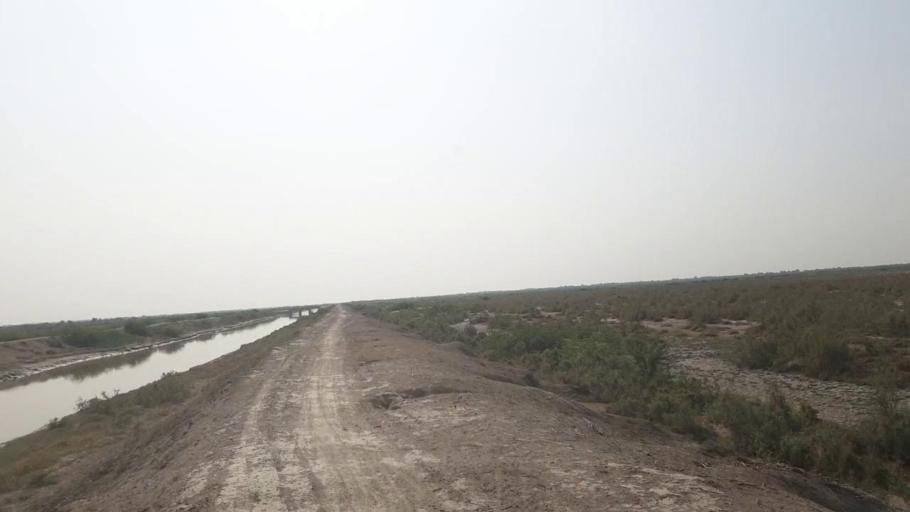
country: PK
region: Sindh
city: Kadhan
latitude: 24.3834
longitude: 68.8990
